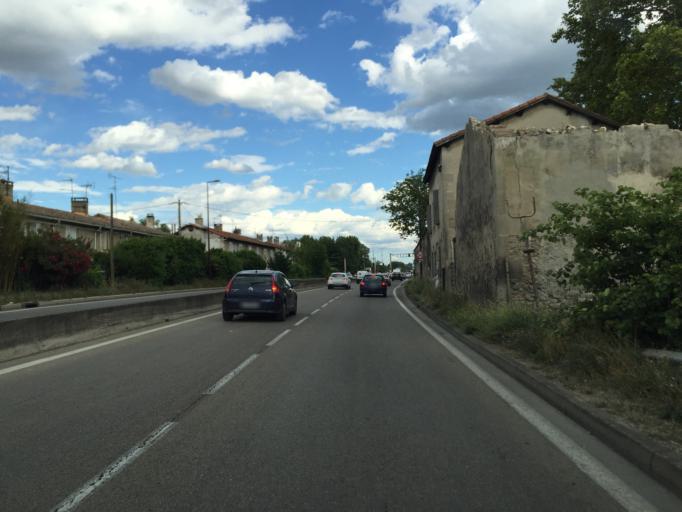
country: FR
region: Provence-Alpes-Cote d'Azur
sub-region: Departement du Vaucluse
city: Montfavet
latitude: 43.9119
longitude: 4.8815
